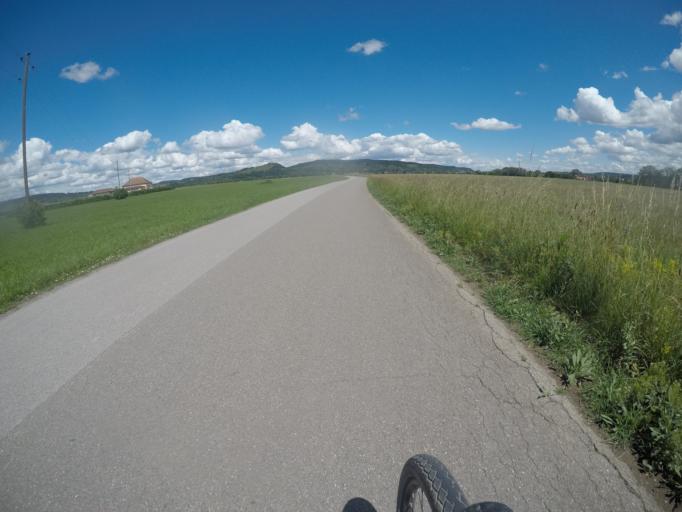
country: DE
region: Baden-Wuerttemberg
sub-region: Tuebingen Region
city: Rottenburg
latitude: 48.4839
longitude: 8.9667
